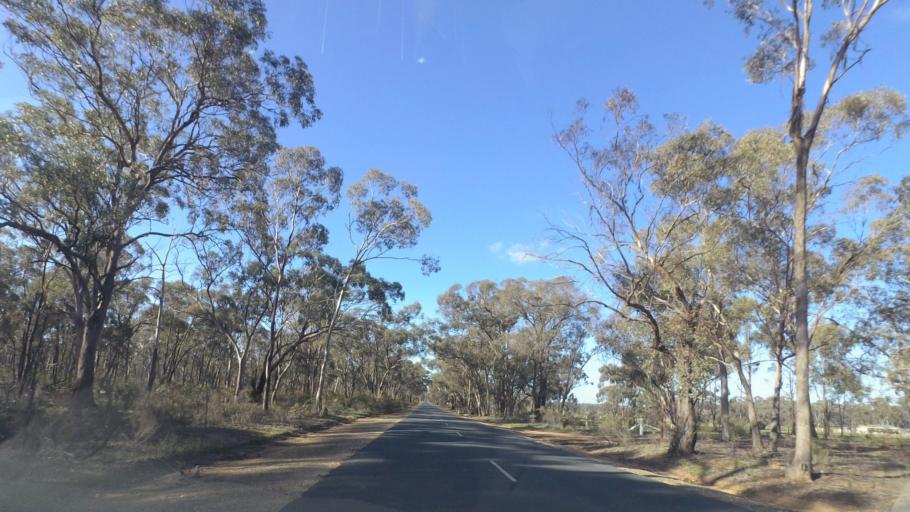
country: AU
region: Victoria
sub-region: Greater Bendigo
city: Epsom
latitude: -36.6636
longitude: 144.4478
